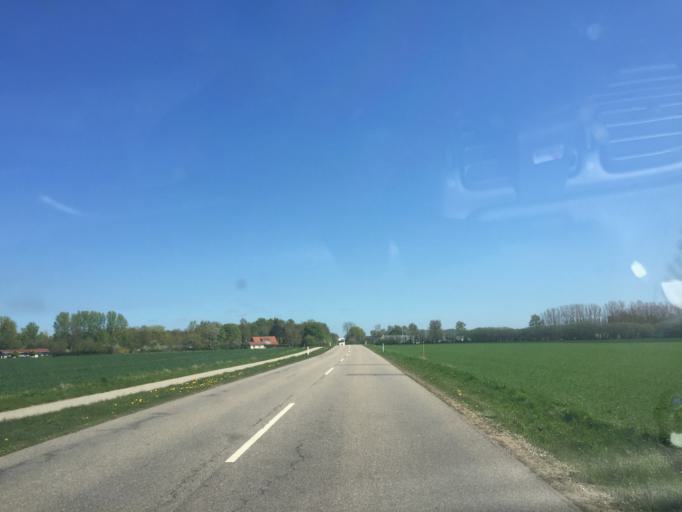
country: DK
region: Capital Region
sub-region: Egedal Kommune
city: Ganlose
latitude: 55.7809
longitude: 12.2423
